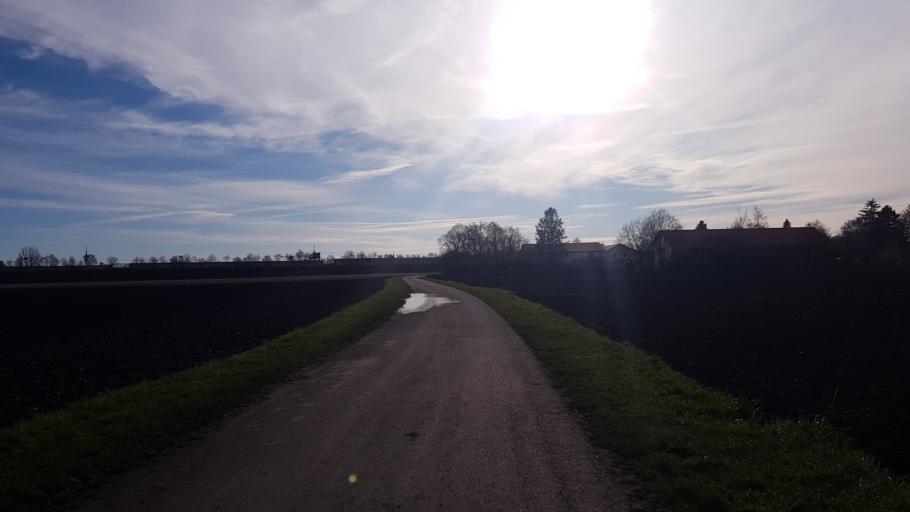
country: DE
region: Bavaria
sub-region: Upper Bavaria
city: Oberschleissheim
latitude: 48.2296
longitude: 11.5302
